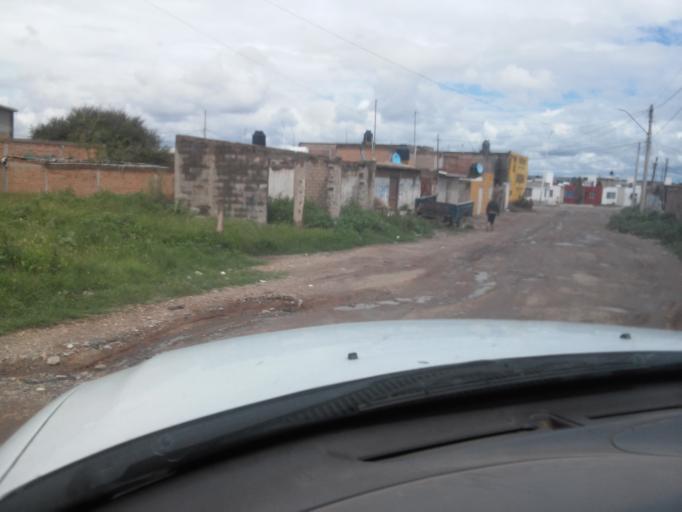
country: MX
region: Durango
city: Victoria de Durango
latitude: 24.0181
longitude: -104.6141
